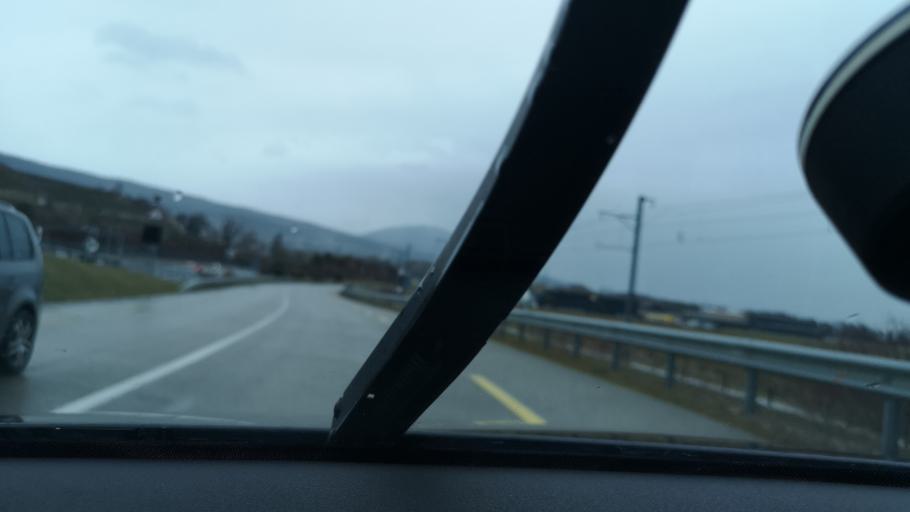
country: CH
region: Neuchatel
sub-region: Boudry District
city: Cortaillod
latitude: 46.9576
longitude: 6.8596
